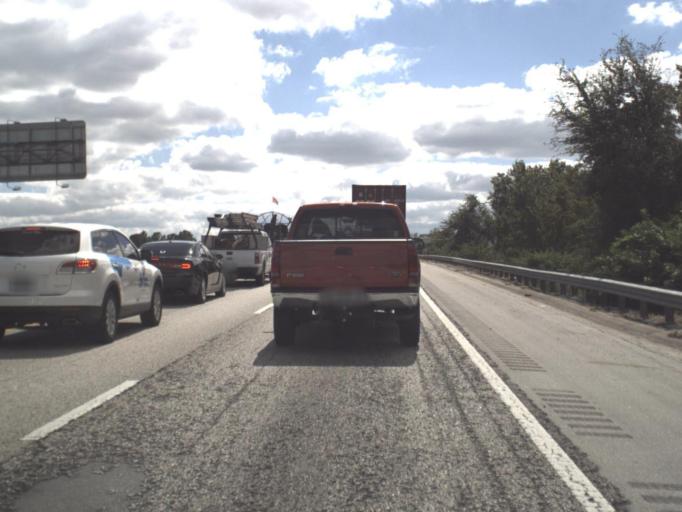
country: US
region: Florida
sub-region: Orange County
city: Southchase
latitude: 28.4098
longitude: -81.3917
